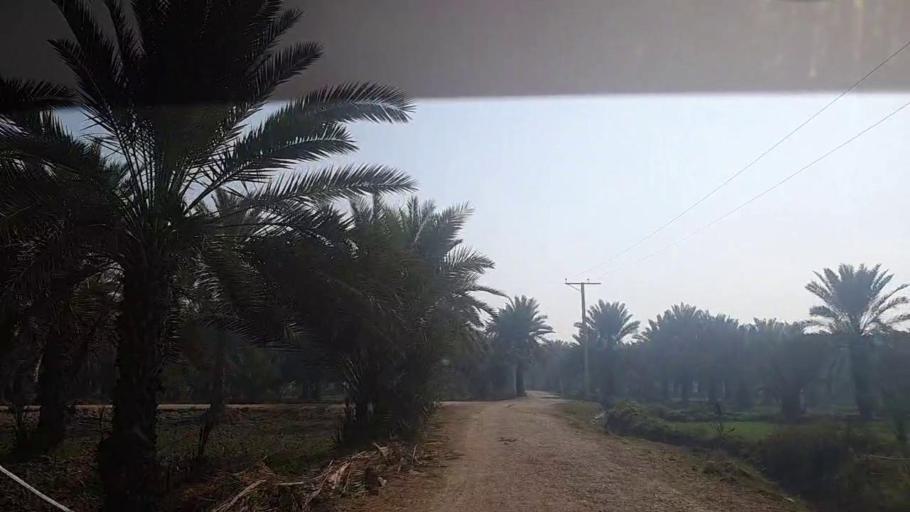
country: PK
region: Sindh
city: Khairpur
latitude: 27.4788
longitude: 68.7197
